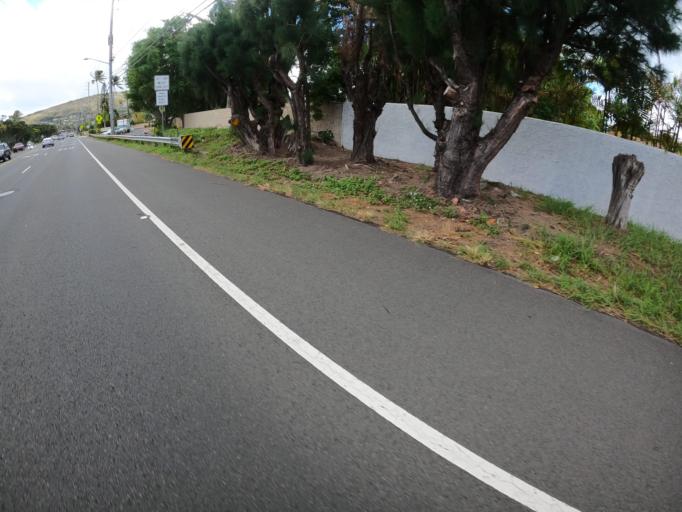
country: US
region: Hawaii
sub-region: Honolulu County
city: Waimanalo Beach
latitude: 21.2795
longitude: -157.7092
